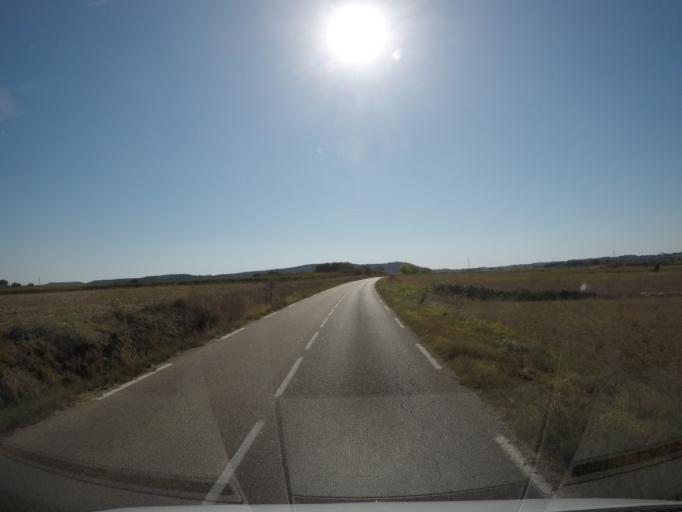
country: FR
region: Languedoc-Roussillon
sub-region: Departement du Gard
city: Ledignan
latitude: 44.0149
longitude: 4.1087
